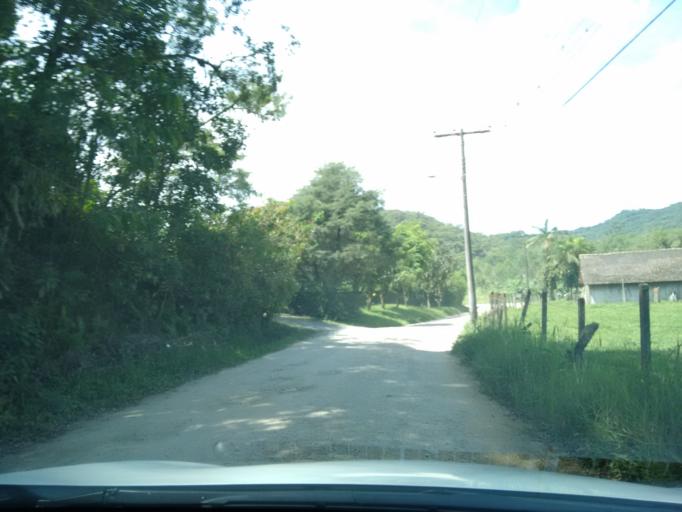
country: BR
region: Santa Catarina
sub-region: Pomerode
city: Pomerode
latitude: -26.6963
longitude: -49.1167
